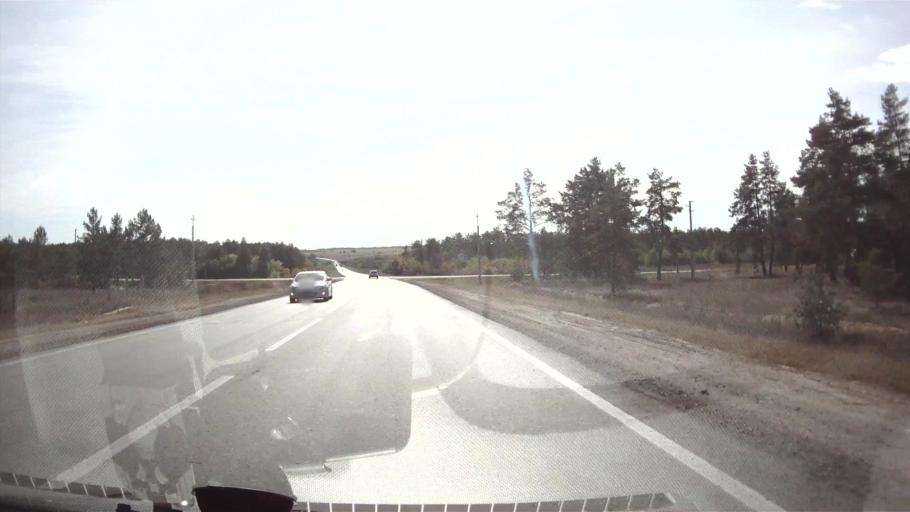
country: RU
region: Samara
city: Varlamovo
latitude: 53.1476
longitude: 48.2844
